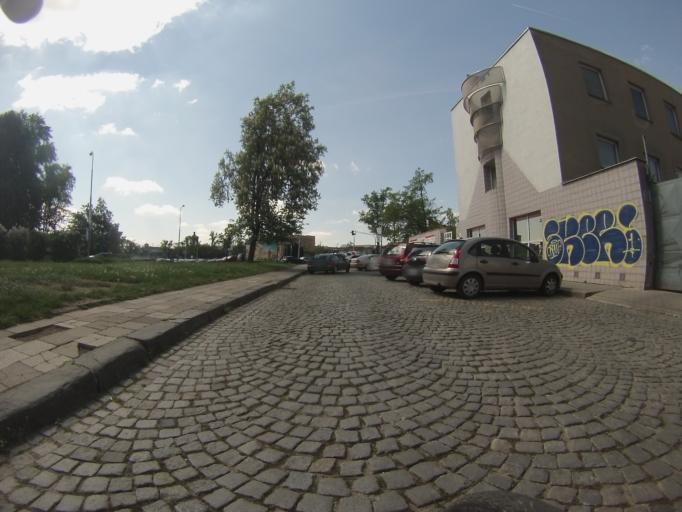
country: CZ
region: South Moravian
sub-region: Mesto Brno
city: Brno
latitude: 49.1878
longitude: 16.6200
